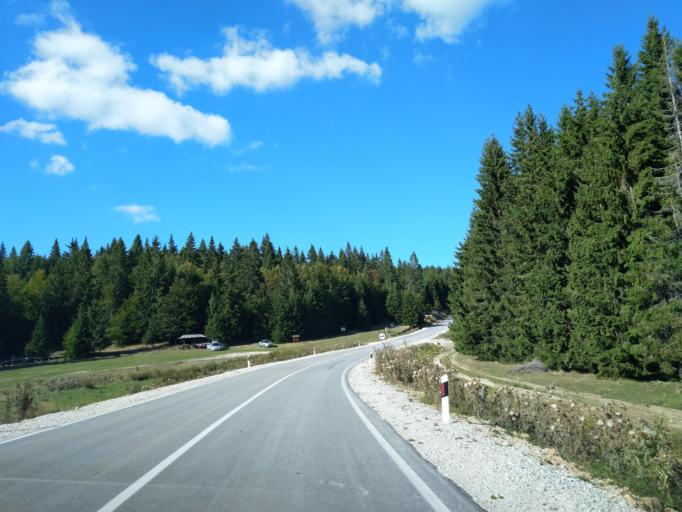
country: RS
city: Sokolovica
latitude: 43.2974
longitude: 20.3062
